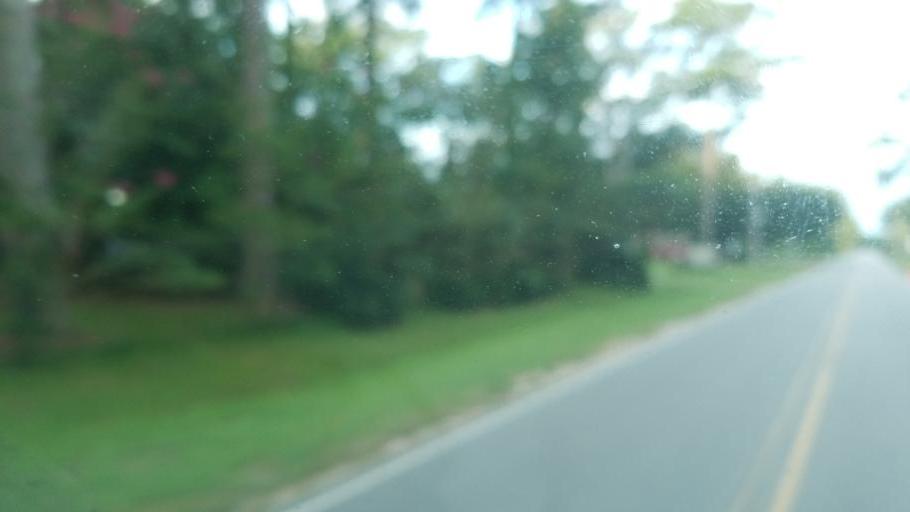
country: US
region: North Carolina
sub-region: Dare County
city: Wanchese
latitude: 35.8420
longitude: -75.6479
